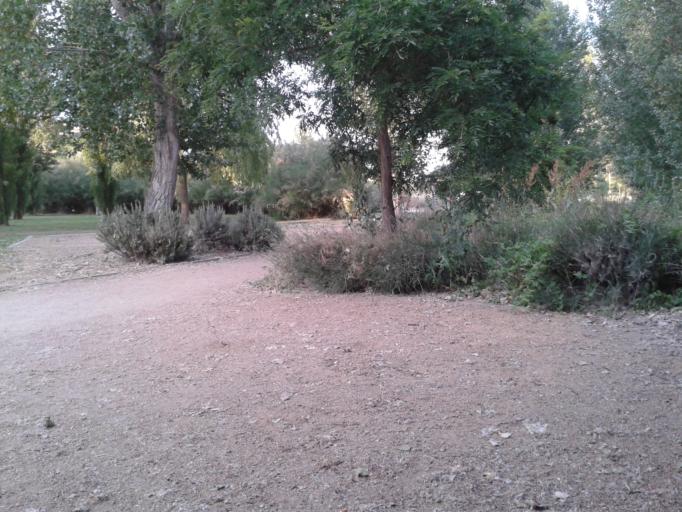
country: ES
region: Castille and Leon
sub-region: Provincia de Valladolid
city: Arroyo
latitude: 41.6080
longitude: -4.7959
